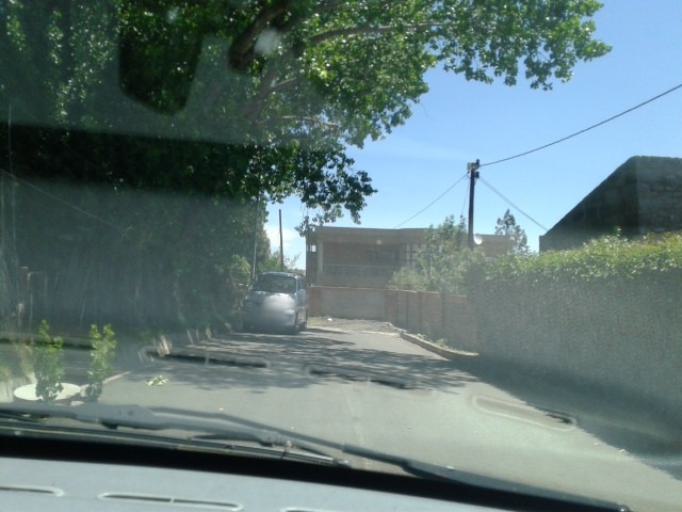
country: LS
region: Maseru
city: Maseru
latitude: -29.3018
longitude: 27.4749
